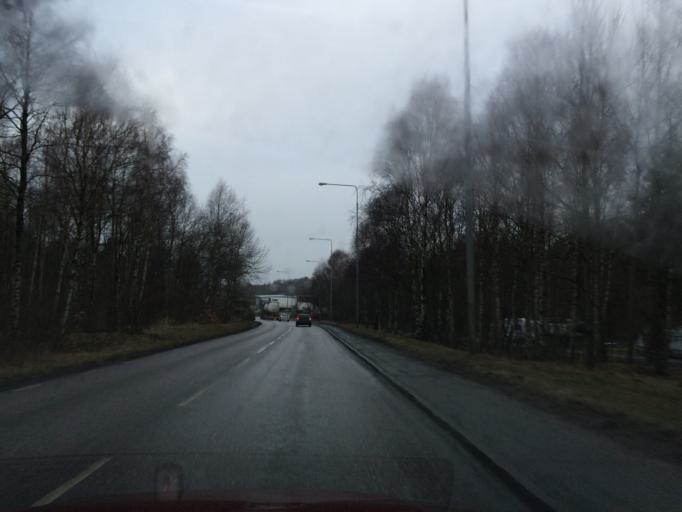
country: SE
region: Vaestra Goetaland
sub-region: Goteborg
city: Torslanda
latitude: 57.7047
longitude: 11.8423
